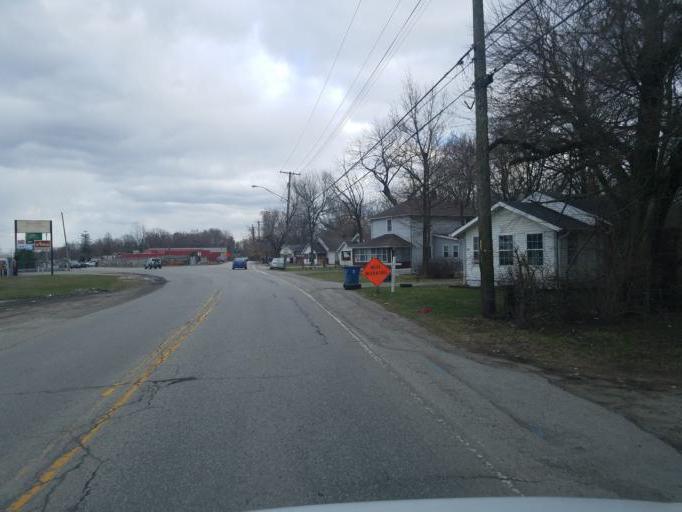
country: US
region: Indiana
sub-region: Marion County
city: Speedway
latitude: 39.7630
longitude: -86.2326
